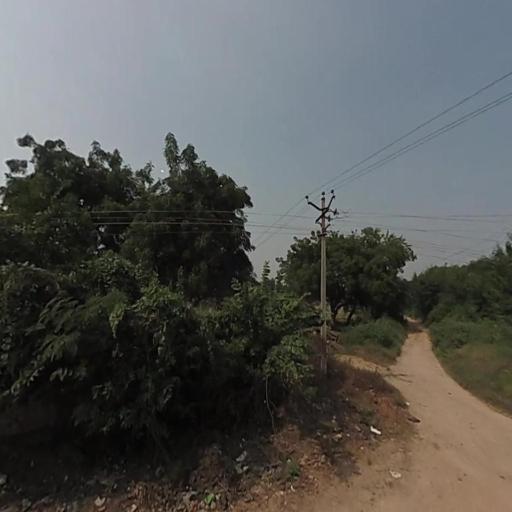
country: IN
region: Telangana
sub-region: Nalgonda
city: Nalgonda
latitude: 17.1893
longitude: 79.1292
